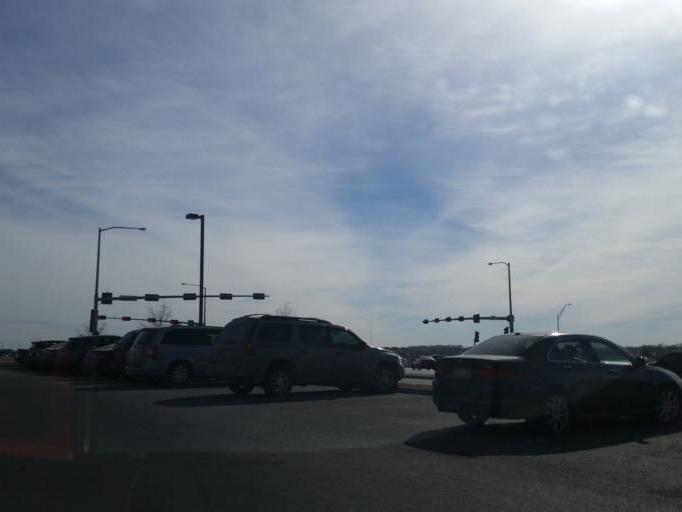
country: US
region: Nebraska
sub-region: Sarpy County
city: Papillion
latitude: 41.1381
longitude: -96.0233
